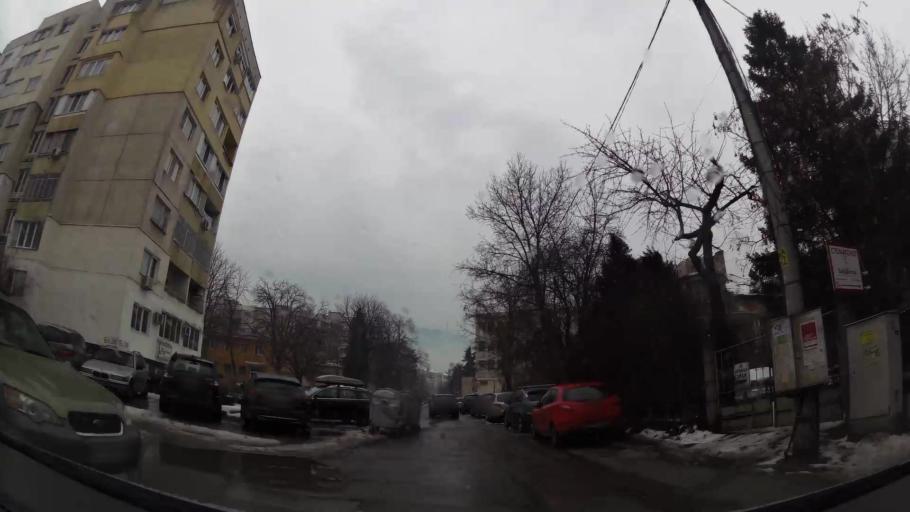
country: BG
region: Sofia-Capital
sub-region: Stolichna Obshtina
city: Sofia
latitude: 42.6684
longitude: 23.2690
